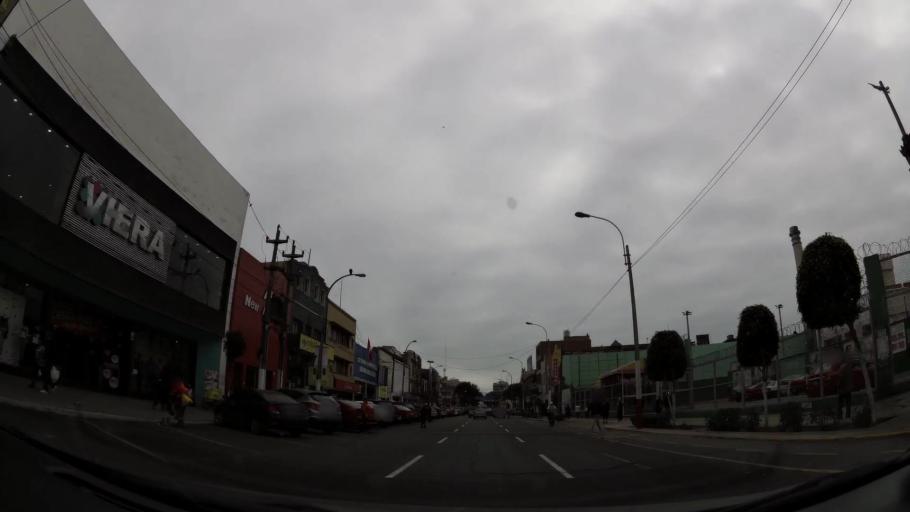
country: PE
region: Callao
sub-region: Callao
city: Callao
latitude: -12.0607
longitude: -77.1415
